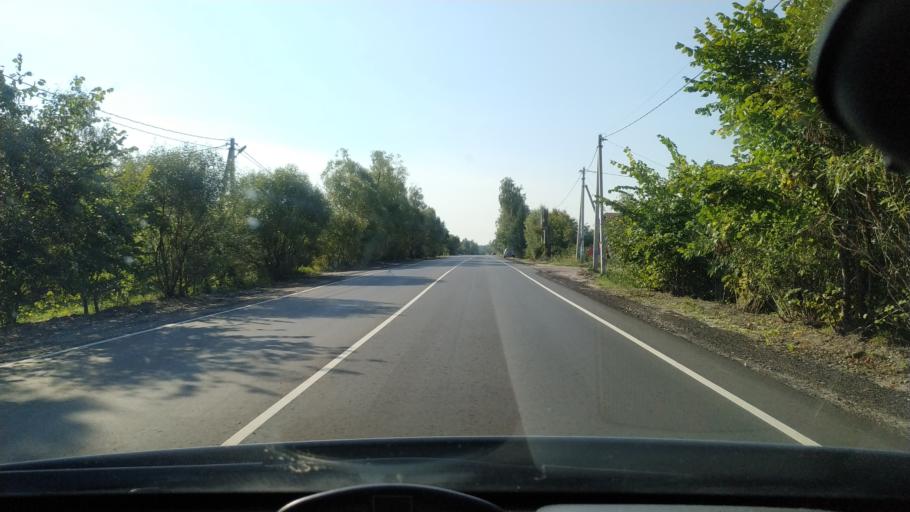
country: RU
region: Moskovskaya
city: Misheronskiy
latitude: 55.6514
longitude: 39.7546
